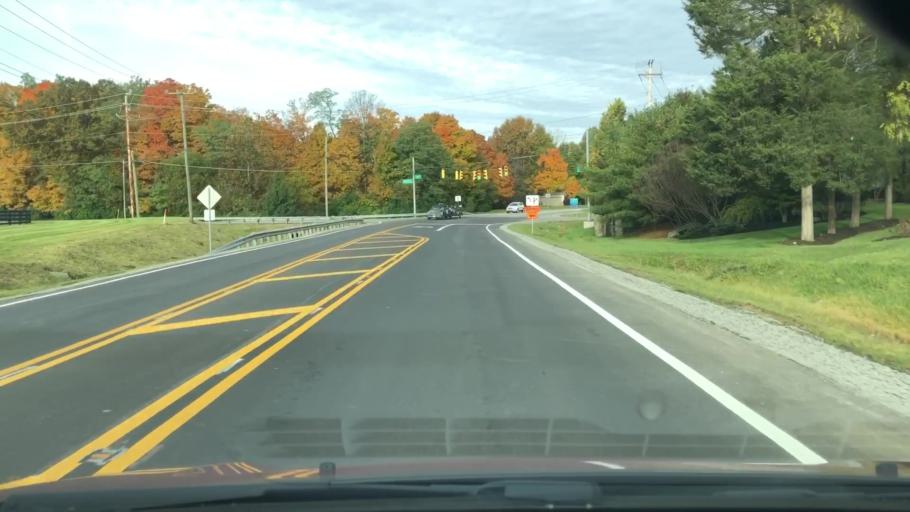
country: US
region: Ohio
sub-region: Franklin County
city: Huber Ridge
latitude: 40.1013
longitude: -82.8658
